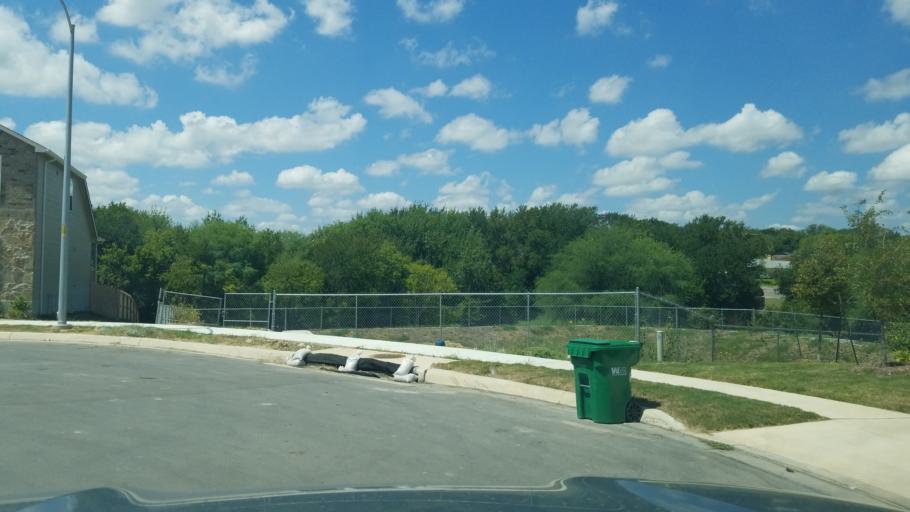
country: US
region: Texas
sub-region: Bexar County
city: Converse
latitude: 29.5355
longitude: -98.3168
